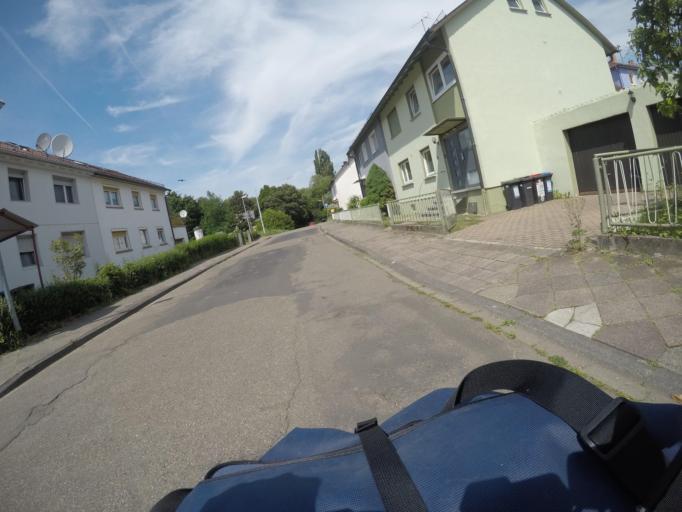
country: DE
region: Baden-Wuerttemberg
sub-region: Karlsruhe Region
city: Karlsruhe
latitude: 49.0034
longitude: 8.4586
